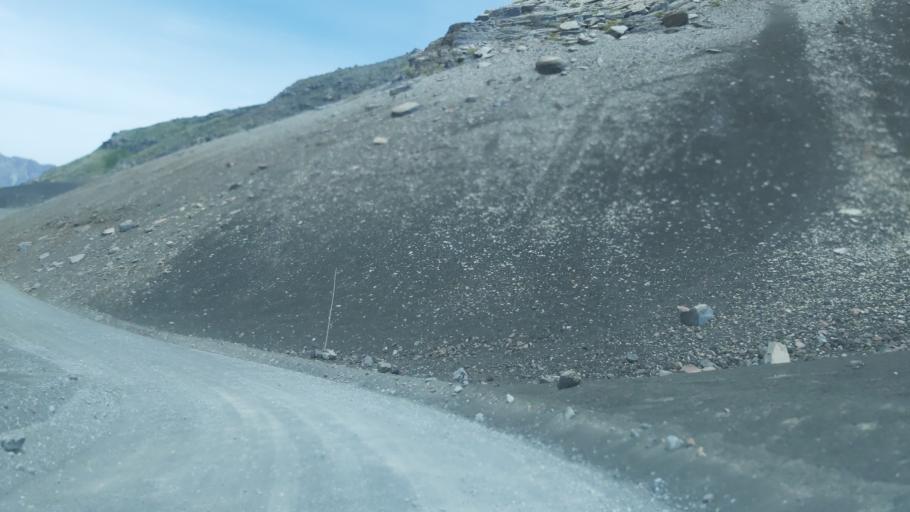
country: AR
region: Neuquen
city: Andacollo
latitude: -37.4054
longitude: -71.3008
